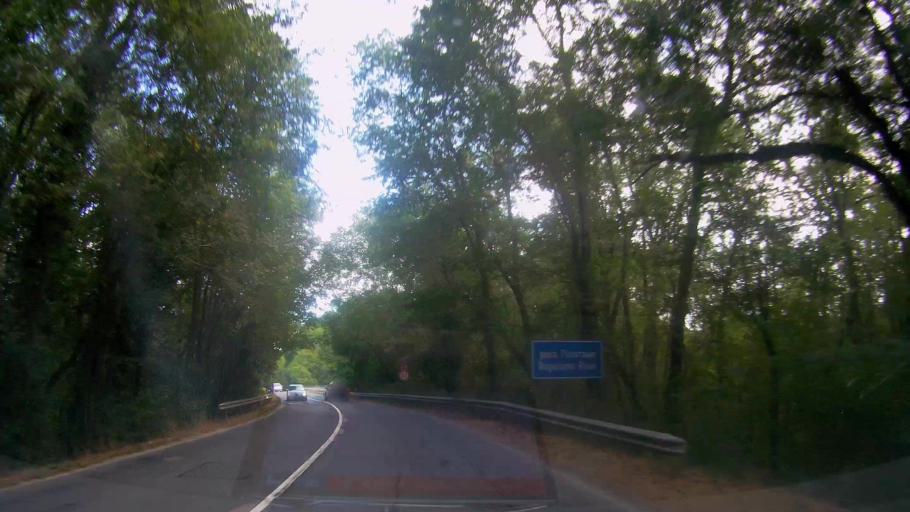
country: BG
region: Burgas
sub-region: Obshtina Primorsko
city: Primorsko
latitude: 42.3023
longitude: 27.7265
